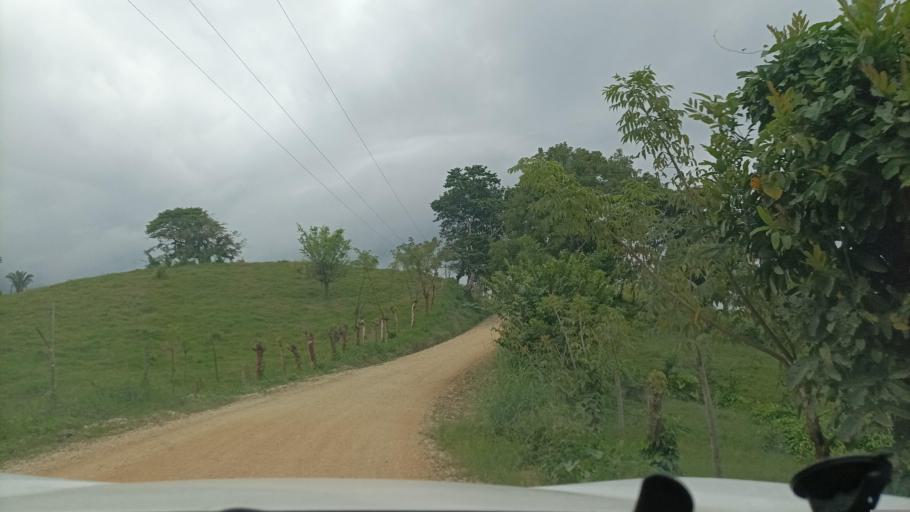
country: MX
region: Veracruz
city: Hidalgotitlan
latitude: 17.6510
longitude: -94.5003
